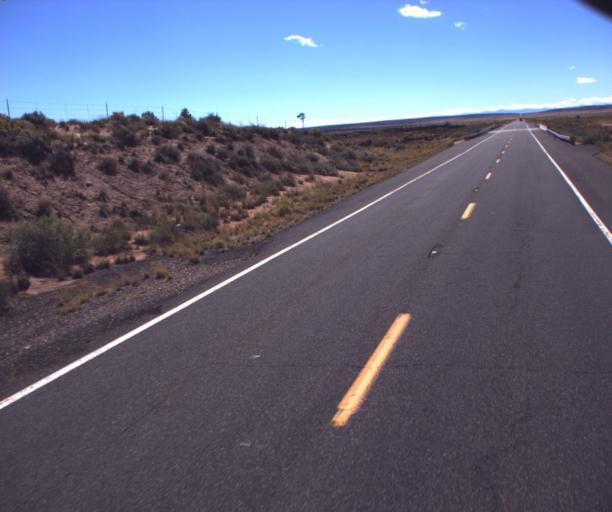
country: US
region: Arizona
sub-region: Apache County
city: Saint Johns
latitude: 34.7184
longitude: -109.2611
